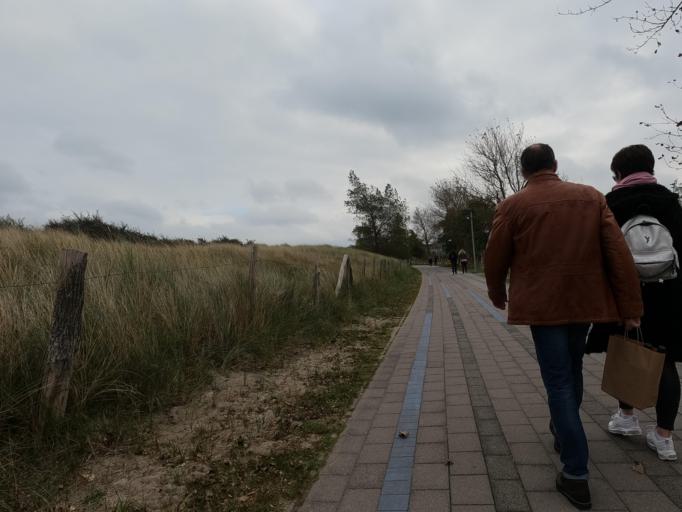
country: DE
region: Schleswig-Holstein
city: Heiligenhafen
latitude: 54.3814
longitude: 10.9725
